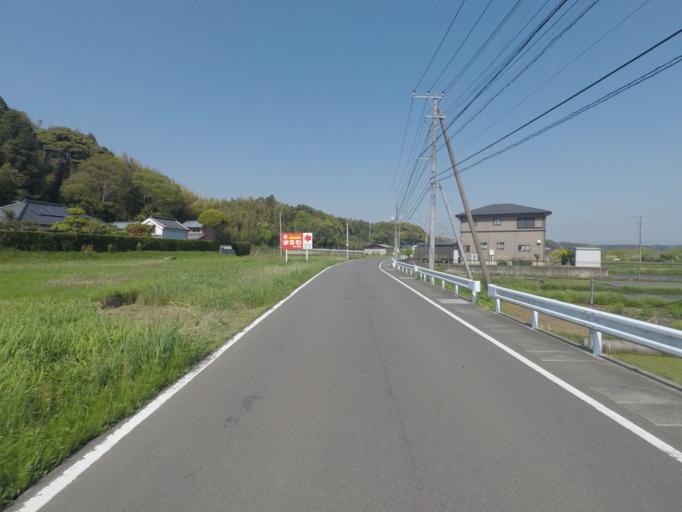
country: JP
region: Ibaraki
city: Ami
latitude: 36.0729
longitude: 140.2551
